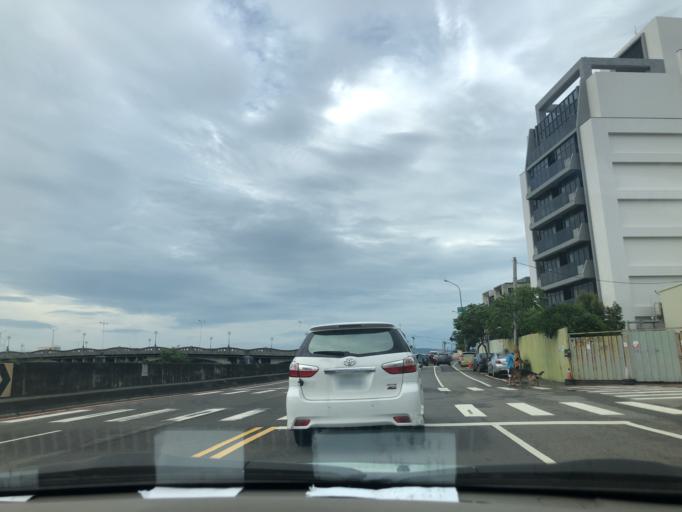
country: TW
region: Taiwan
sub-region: Taichung City
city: Taichung
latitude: 24.1089
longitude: 120.6979
